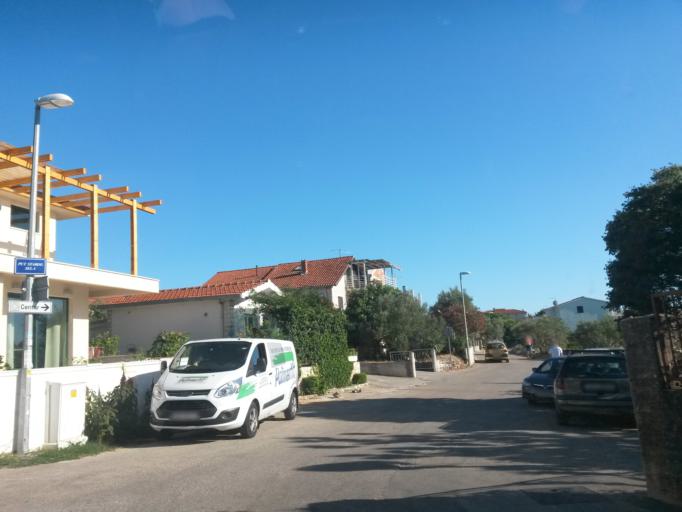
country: HR
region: Sibensko-Kniniska
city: Rogoznica
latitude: 43.5405
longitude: 15.9610
